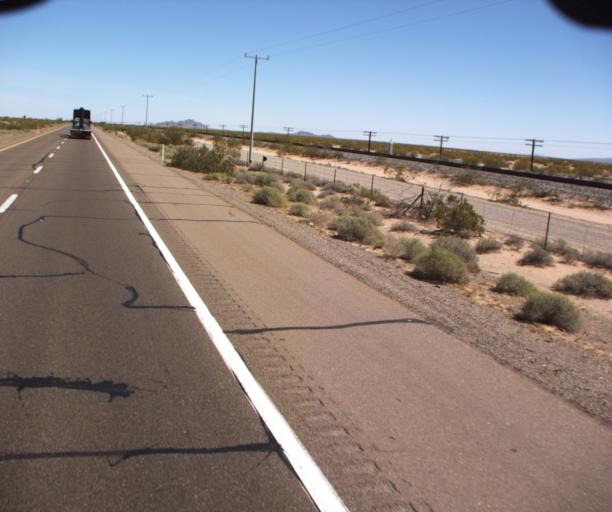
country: US
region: Arizona
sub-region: Yuma County
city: Wellton
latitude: 32.7632
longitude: -113.6281
